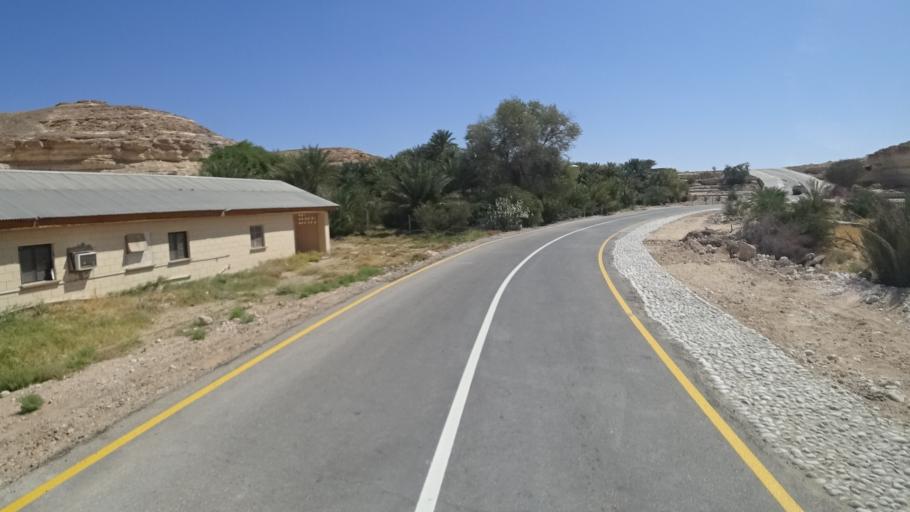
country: OM
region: Zufar
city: Salalah
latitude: 17.4785
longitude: 53.3522
